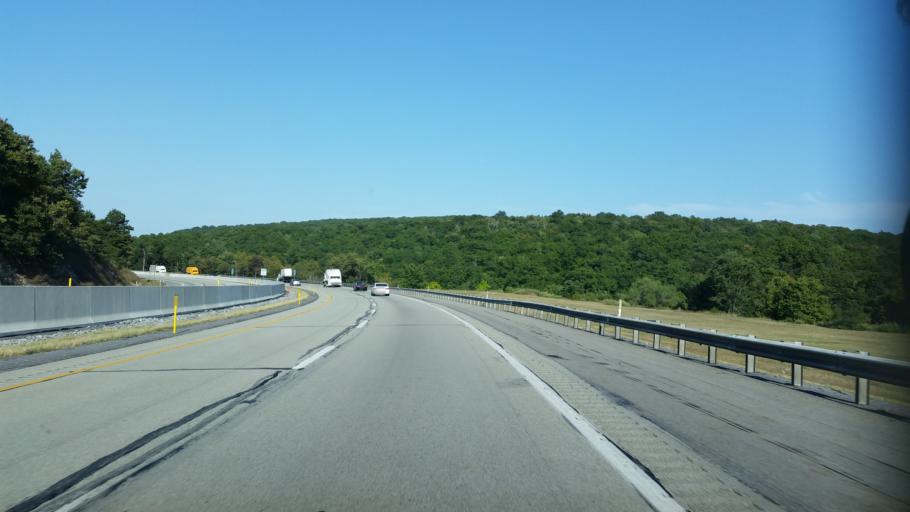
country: US
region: Pennsylvania
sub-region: Fulton County
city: McConnellsburg
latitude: 40.0329
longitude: -78.1345
